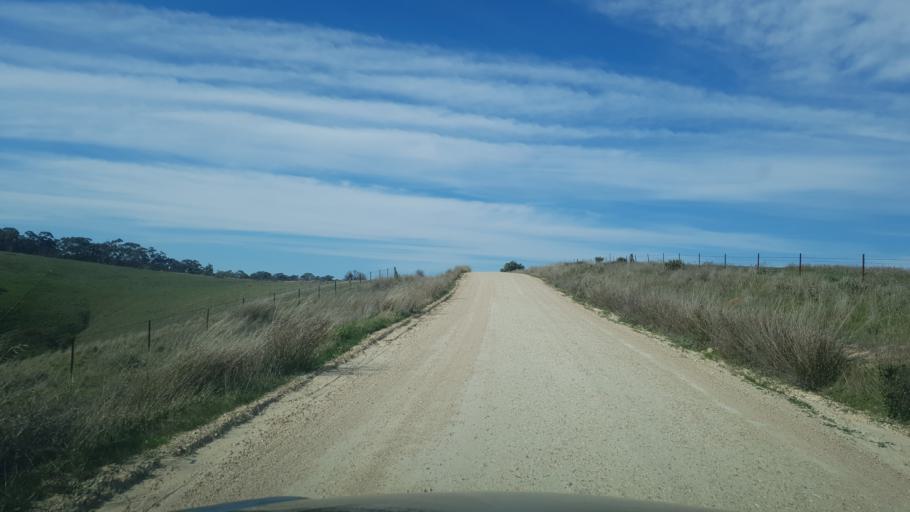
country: AU
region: South Australia
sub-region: Gawler
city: Gawler
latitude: -34.6384
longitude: 138.8049
